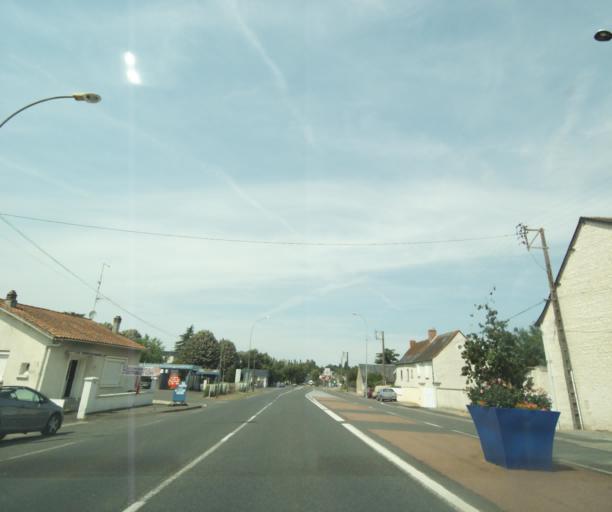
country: FR
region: Centre
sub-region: Departement d'Indre-et-Loire
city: Sainte-Maure-de-Touraine
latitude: 47.1069
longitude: 0.6135
